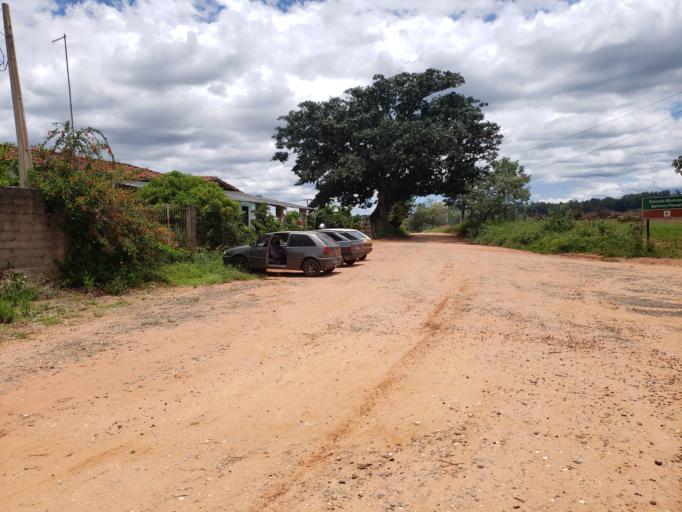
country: BR
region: Sao Paulo
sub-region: Santo Antonio Do Jardim
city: Espirito Santo do Pinhal
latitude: -22.2072
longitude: -46.8363
